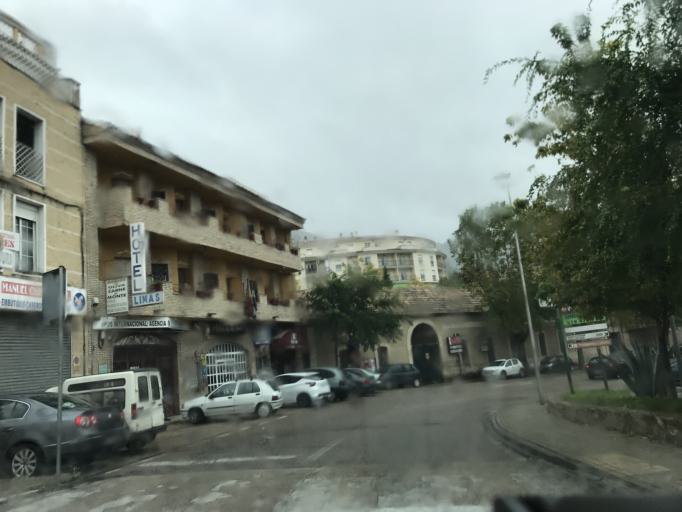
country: ES
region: Andalusia
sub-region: Provincia de Jaen
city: Cazorla
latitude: 37.9145
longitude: -3.0068
